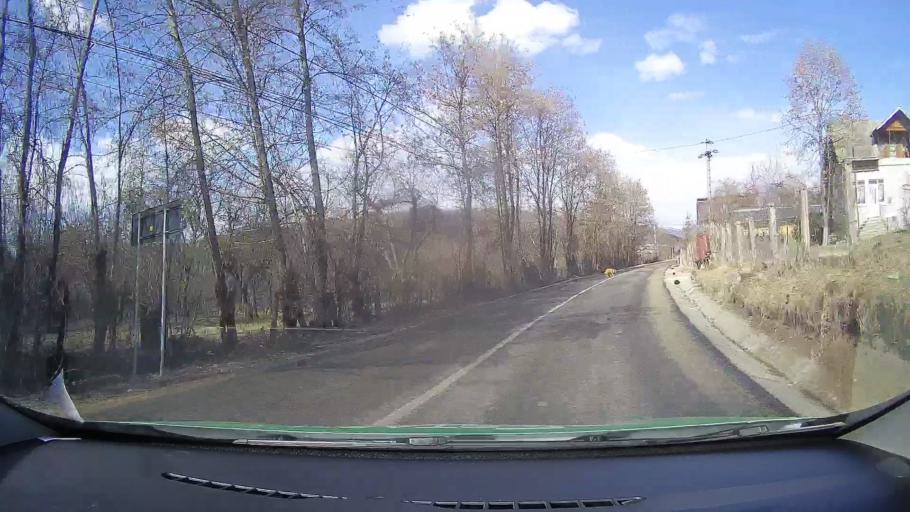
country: RO
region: Dambovita
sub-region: Comuna Runcu
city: Badeni
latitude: 45.1450
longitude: 25.4033
